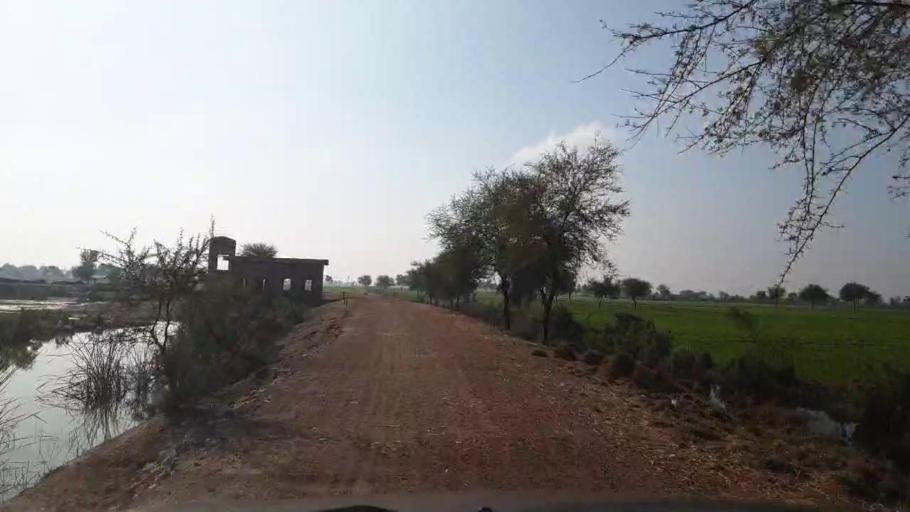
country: PK
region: Sindh
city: Sinjhoro
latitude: 26.0502
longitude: 68.7833
